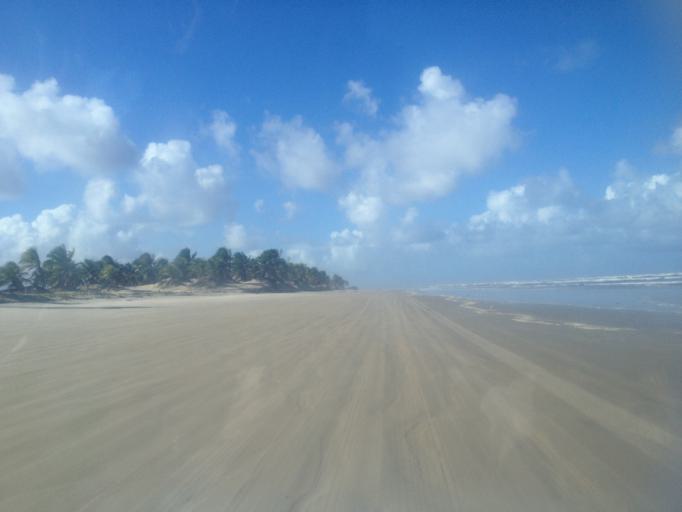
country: BR
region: Sergipe
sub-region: Indiaroba
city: Indiaroba
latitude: -11.4729
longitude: -37.3595
